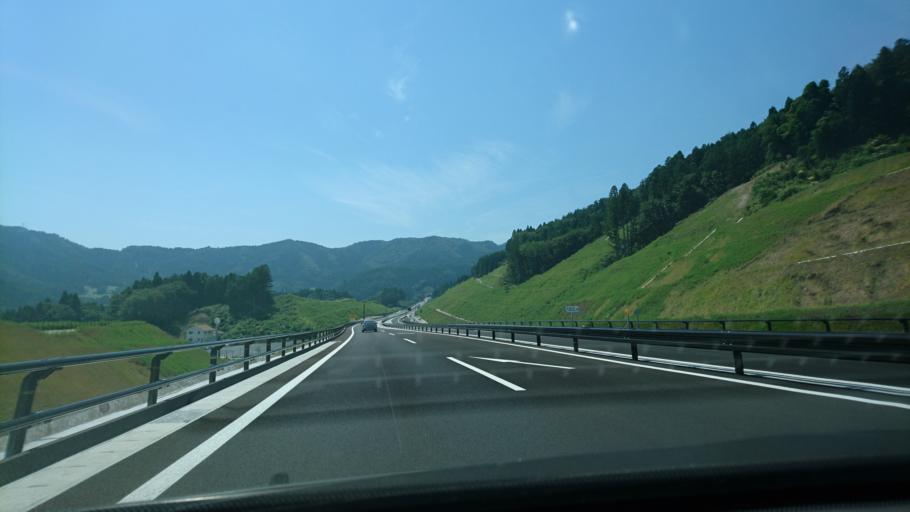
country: JP
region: Iwate
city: Kamaishi
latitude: 39.1508
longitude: 141.8305
